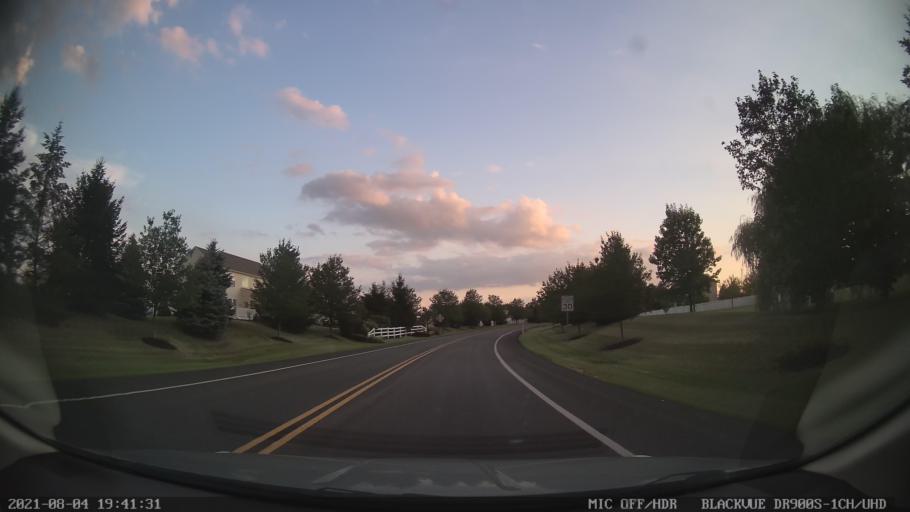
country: US
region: Pennsylvania
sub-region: Lehigh County
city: Breinigsville
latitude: 40.5343
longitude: -75.6215
